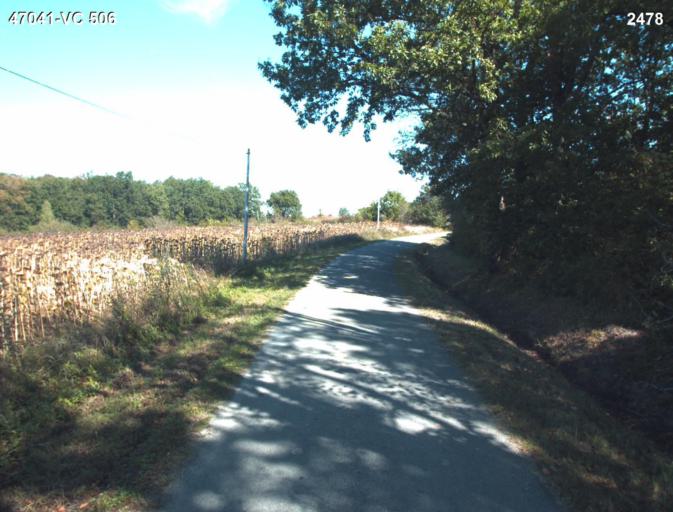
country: FR
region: Aquitaine
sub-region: Departement du Lot-et-Garonne
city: Port-Sainte-Marie
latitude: 44.1952
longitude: 0.3845
